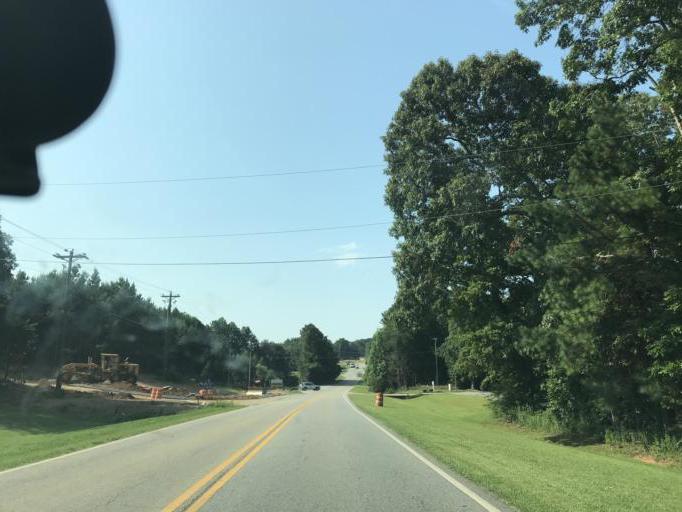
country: US
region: Georgia
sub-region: Forsyth County
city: Cumming
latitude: 34.2334
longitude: -84.1043
